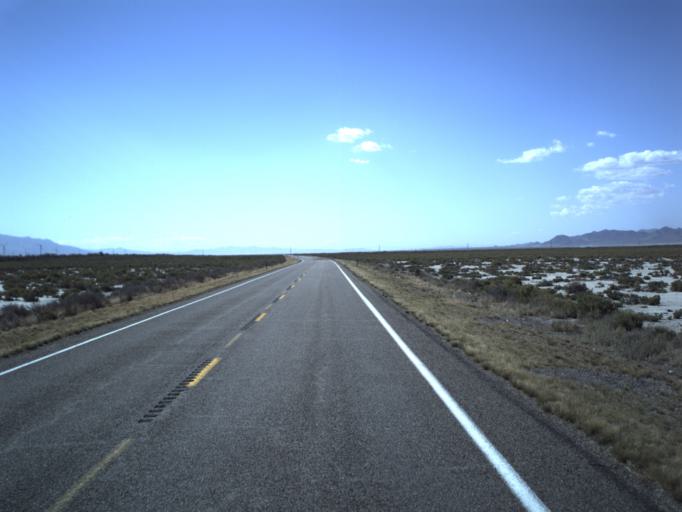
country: US
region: Utah
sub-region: Beaver County
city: Milford
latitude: 38.6039
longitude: -112.9869
